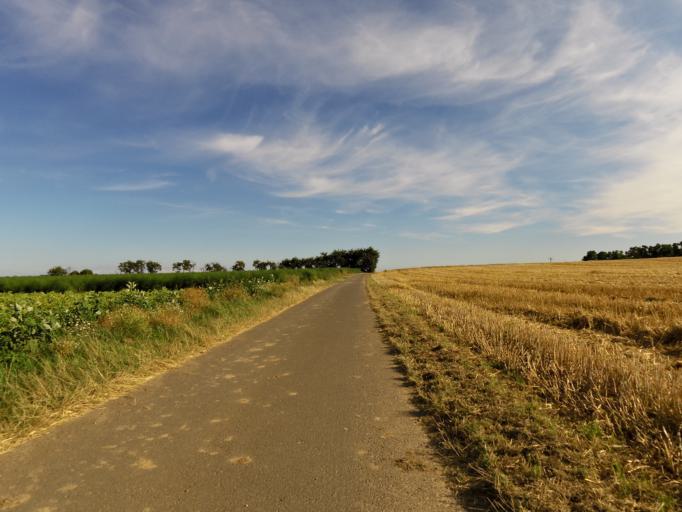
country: DE
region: Rheinland-Pfalz
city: Bissersheim
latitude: 49.5351
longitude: 8.1947
